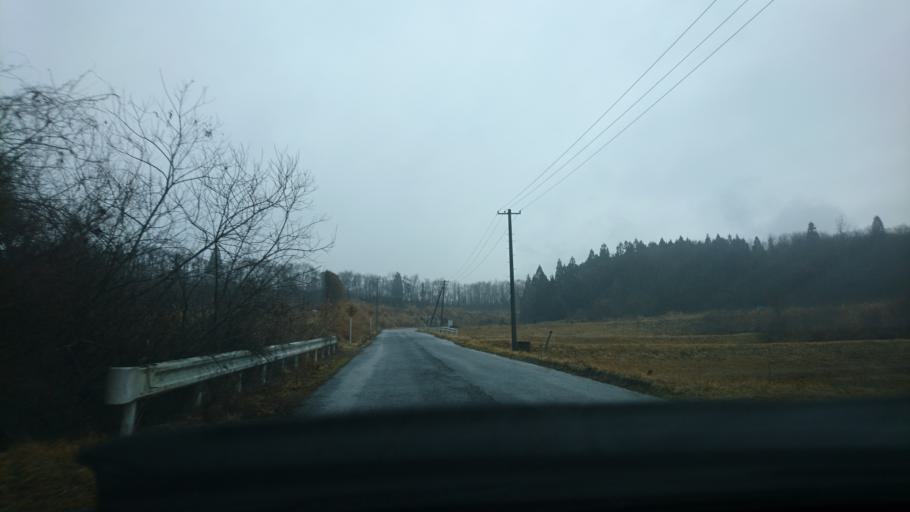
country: JP
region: Iwate
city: Ichinoseki
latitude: 38.8980
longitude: 141.3482
